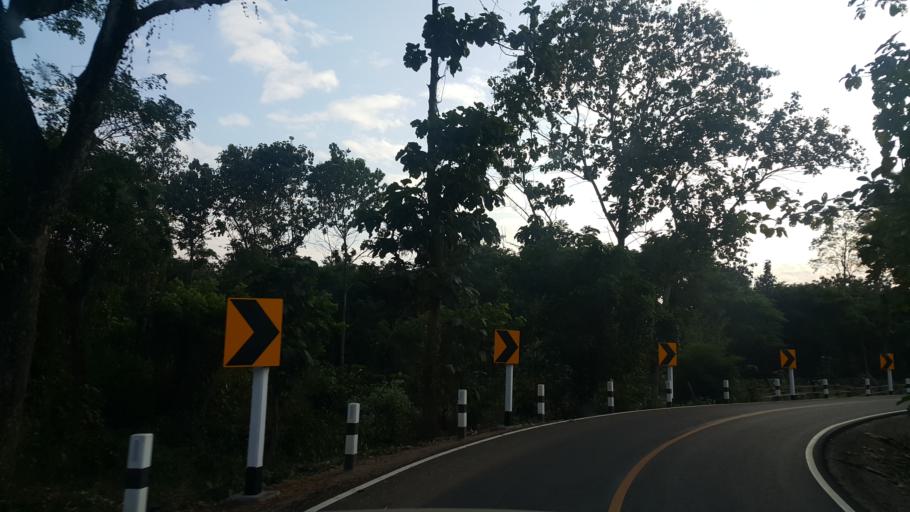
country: TH
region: Lampang
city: Sop Prap
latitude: 17.9299
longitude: 99.3383
